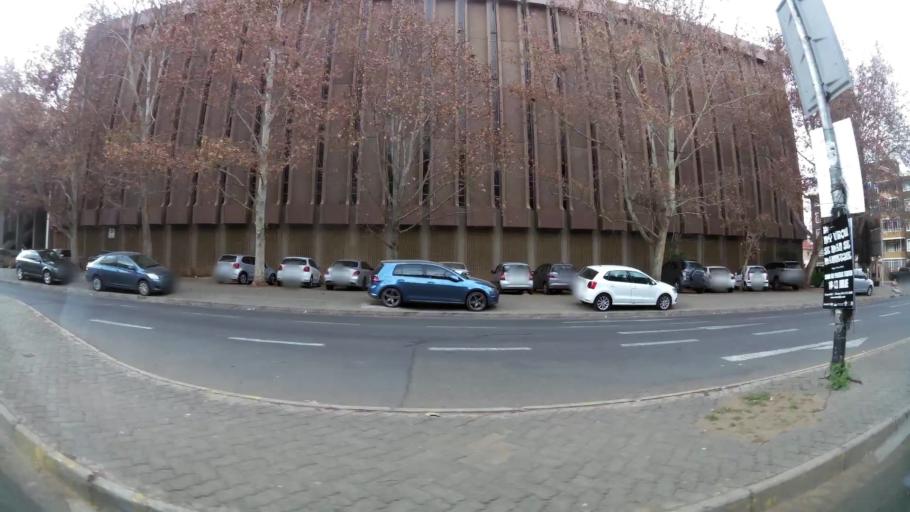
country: ZA
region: Orange Free State
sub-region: Mangaung Metropolitan Municipality
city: Bloemfontein
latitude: -29.1159
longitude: 26.2115
